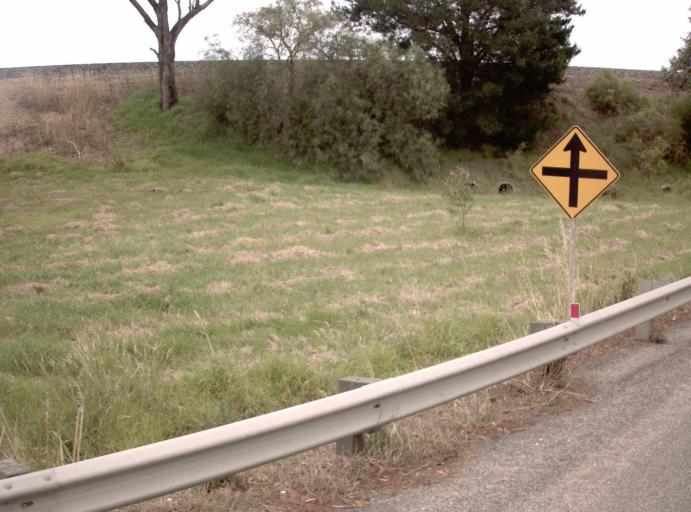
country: AU
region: Victoria
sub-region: Wellington
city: Sale
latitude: -37.9784
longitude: 147.0727
